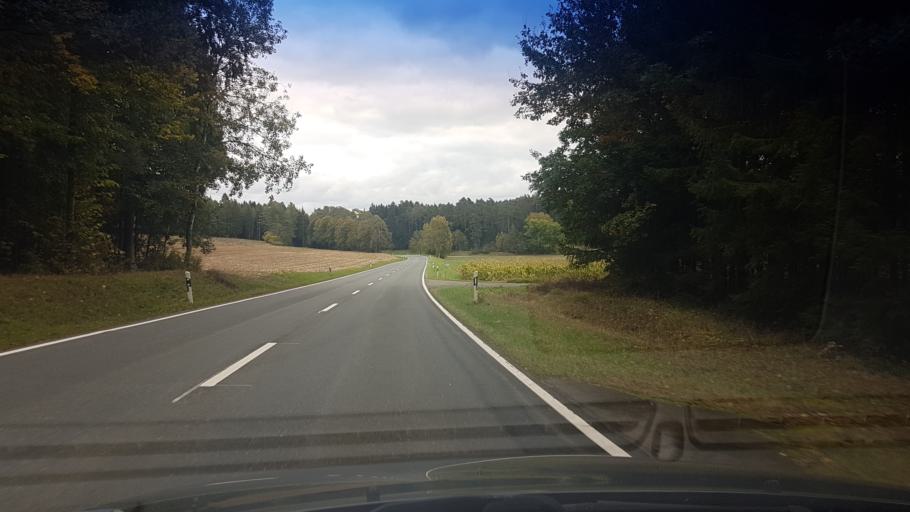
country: DE
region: Bavaria
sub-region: Upper Franconia
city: Stadelhofen
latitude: 50.0105
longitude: 11.2138
